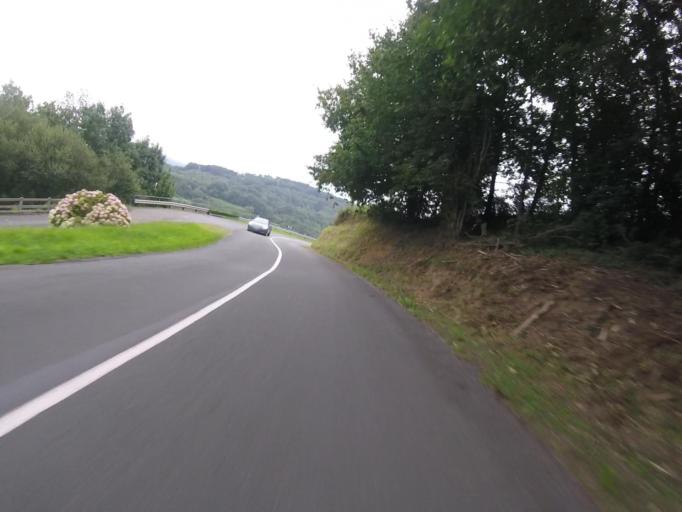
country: ES
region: Basque Country
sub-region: Provincia de Guipuzcoa
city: Lezo
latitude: 43.3120
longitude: -1.8536
